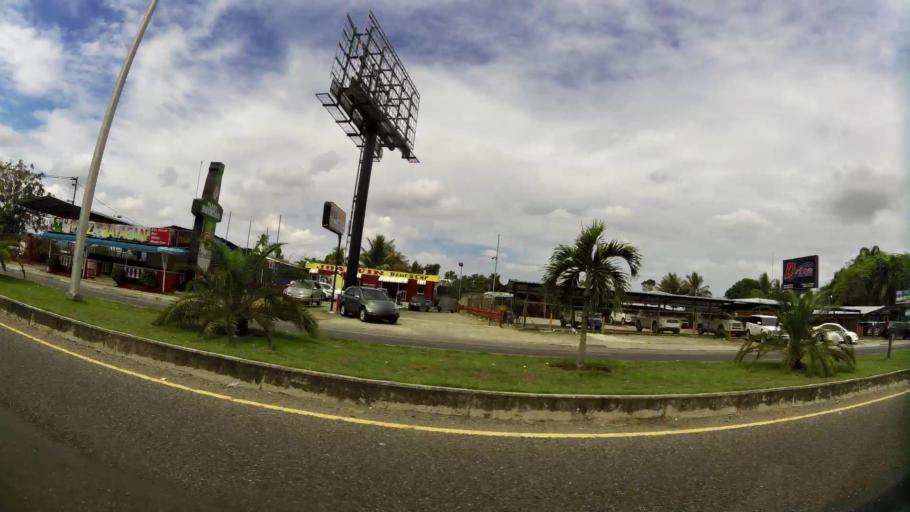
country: DO
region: Santiago
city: Licey al Medio
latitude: 19.3993
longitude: -70.6026
